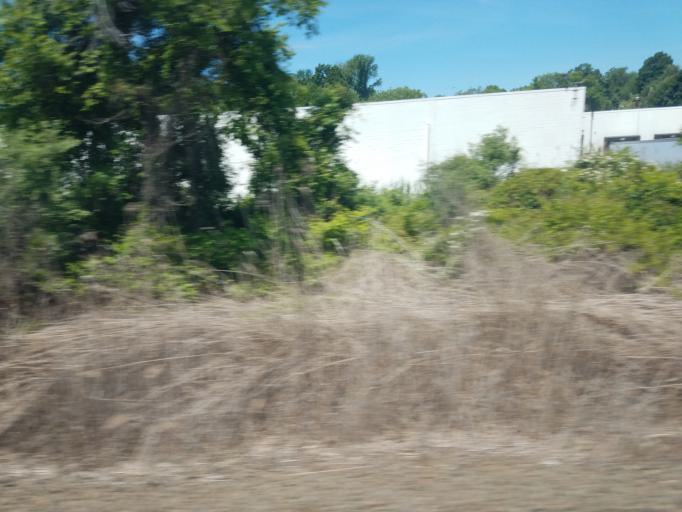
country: US
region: Connecticut
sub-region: New Haven County
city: Hamden
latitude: 41.3598
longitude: -72.8873
